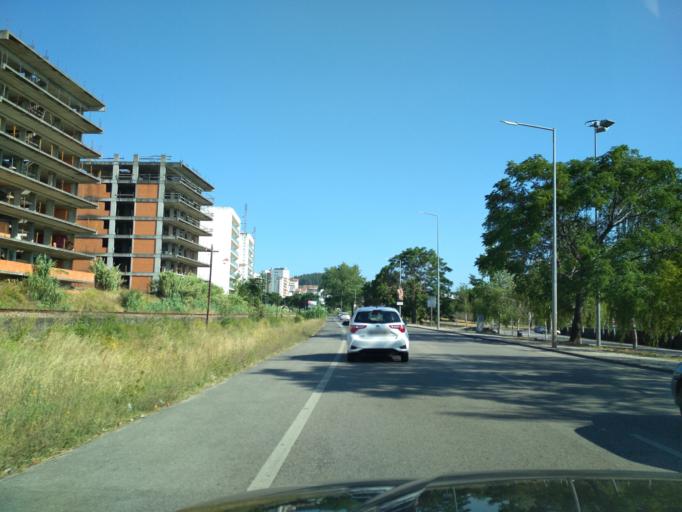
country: PT
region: Coimbra
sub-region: Coimbra
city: Coimbra
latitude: 40.2013
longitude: -8.4241
